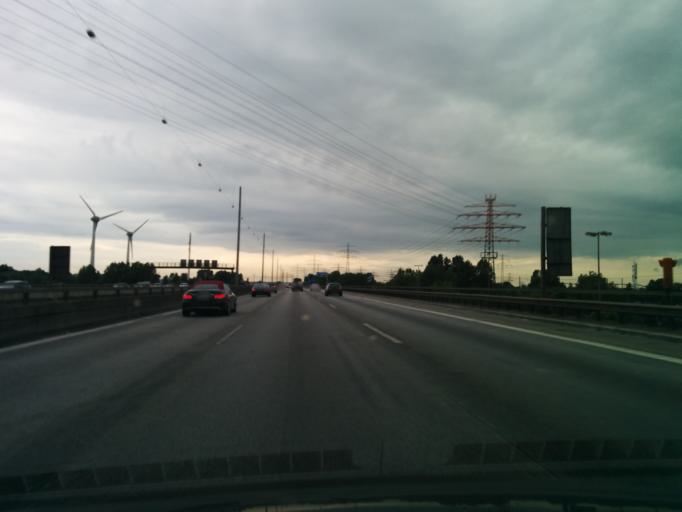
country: DE
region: Hamburg
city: Altona
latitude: 53.5212
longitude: 9.9250
